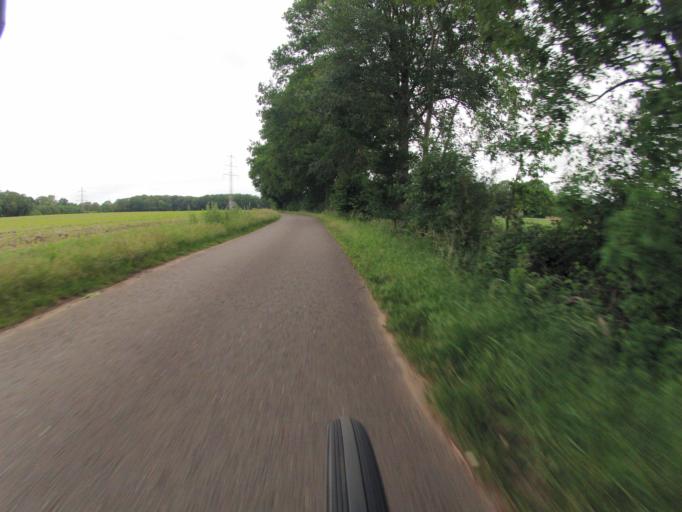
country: DE
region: North Rhine-Westphalia
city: Emsdetten
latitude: 52.2228
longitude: 7.5193
